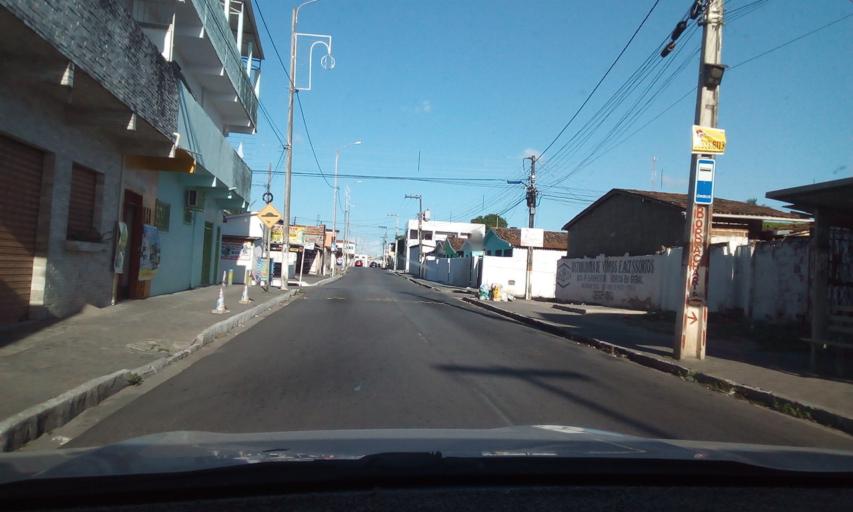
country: BR
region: Paraiba
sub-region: Bayeux
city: Bayeux
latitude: -7.1228
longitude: -34.9088
